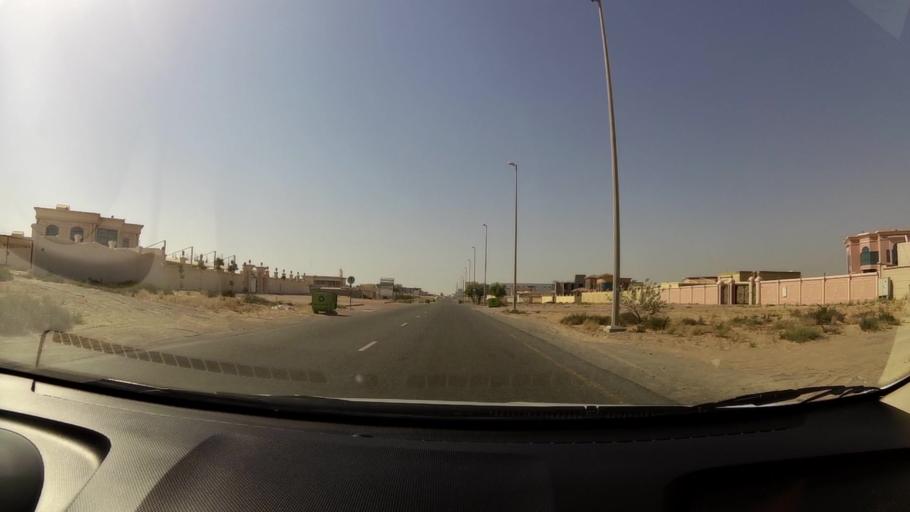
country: AE
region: Umm al Qaywayn
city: Umm al Qaywayn
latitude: 25.4874
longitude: 55.6012
